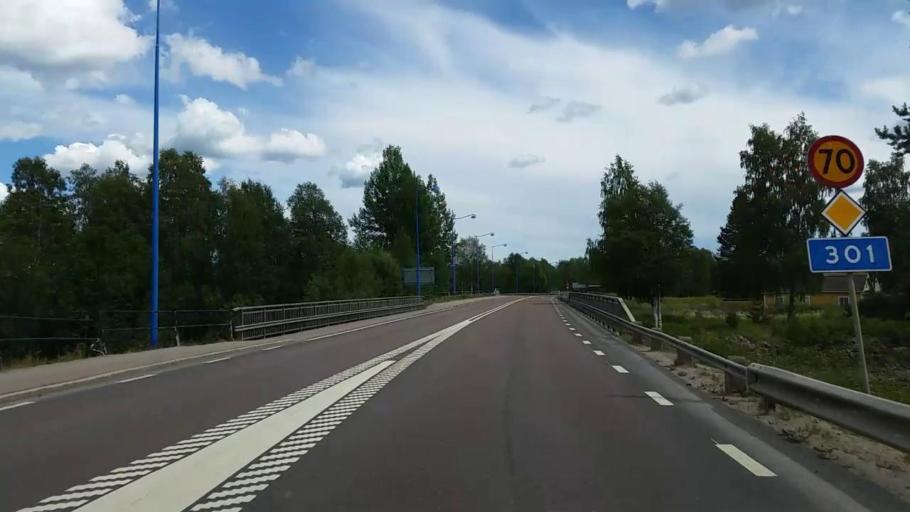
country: SE
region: Gaevleborg
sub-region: Ovanakers Kommun
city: Edsbyn
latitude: 61.3835
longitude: 15.8243
